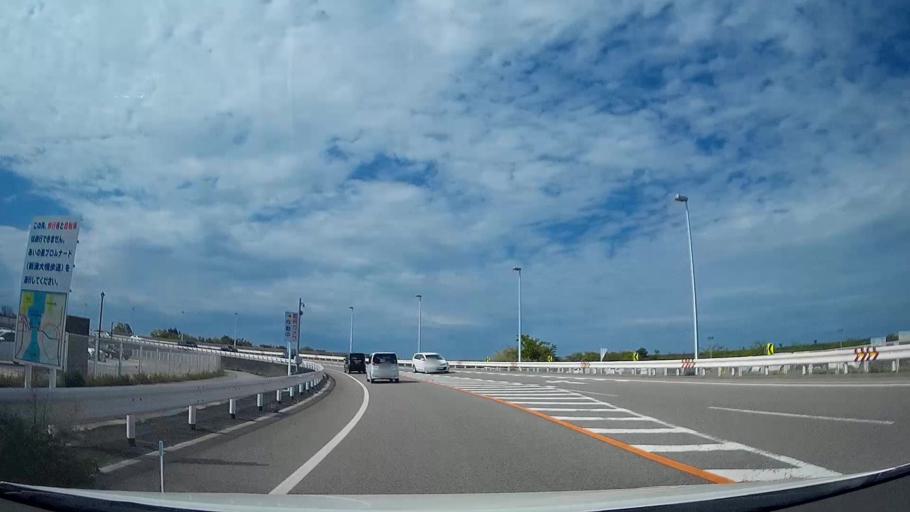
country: JP
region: Toyama
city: Nishishinminato
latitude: 36.7803
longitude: 137.1061
